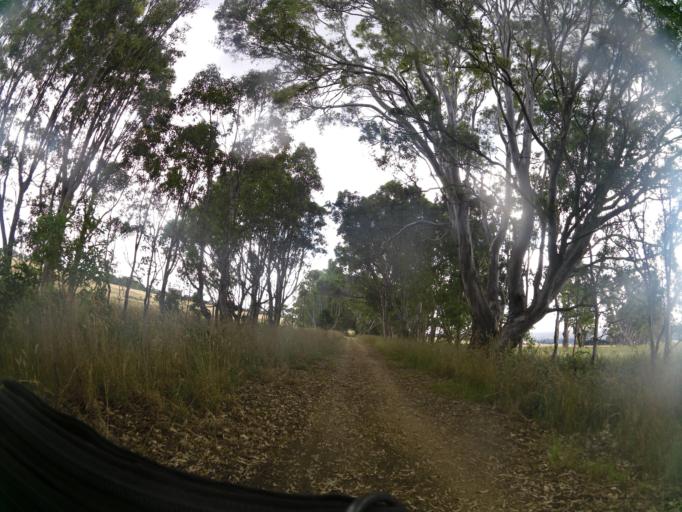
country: AU
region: Victoria
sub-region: Wellington
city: Heyfield
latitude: -38.0213
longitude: 146.6788
